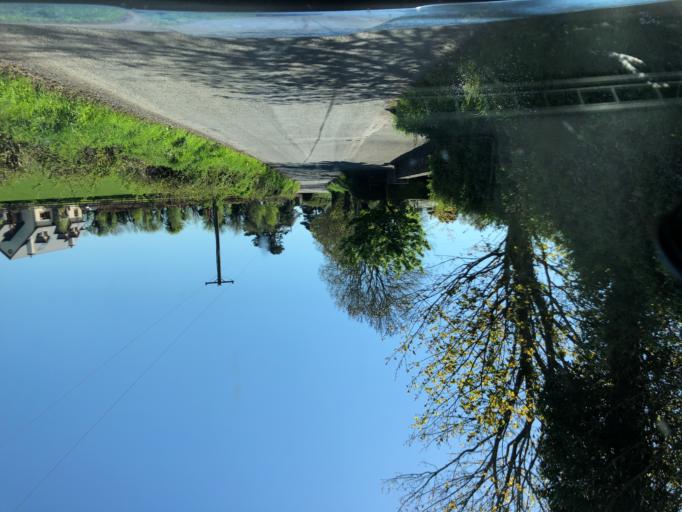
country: IE
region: Connaught
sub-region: County Galway
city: Portumna
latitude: 53.1541
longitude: -8.2952
